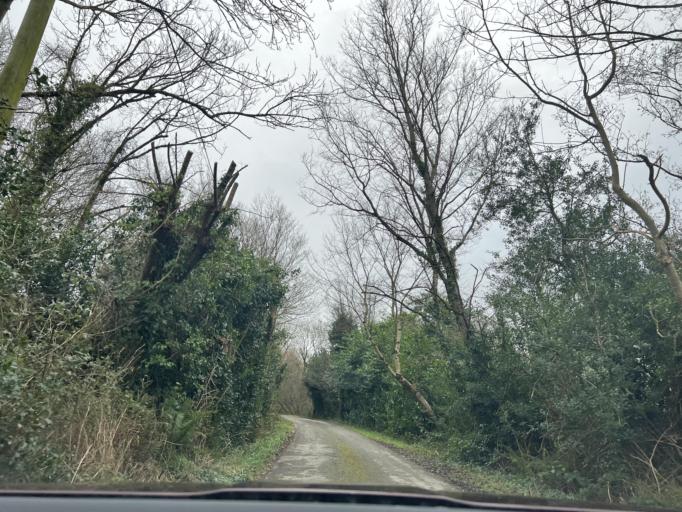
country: IE
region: Leinster
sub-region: Loch Garman
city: Castlebridge
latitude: 52.3868
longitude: -6.5493
